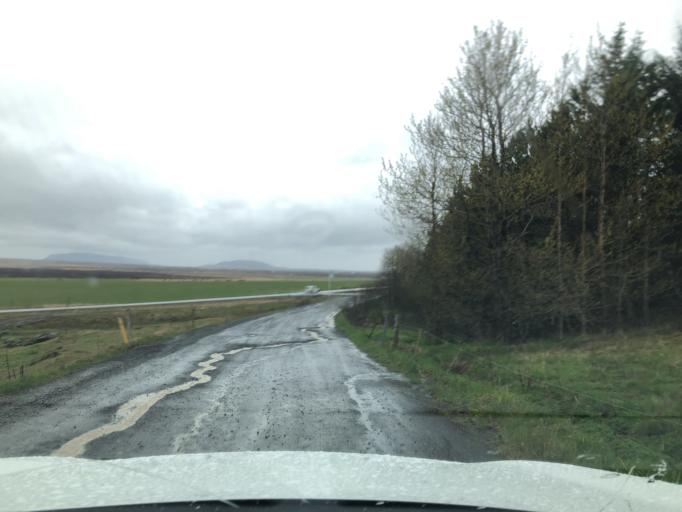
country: IS
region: South
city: Selfoss
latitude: 64.2404
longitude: -20.5493
